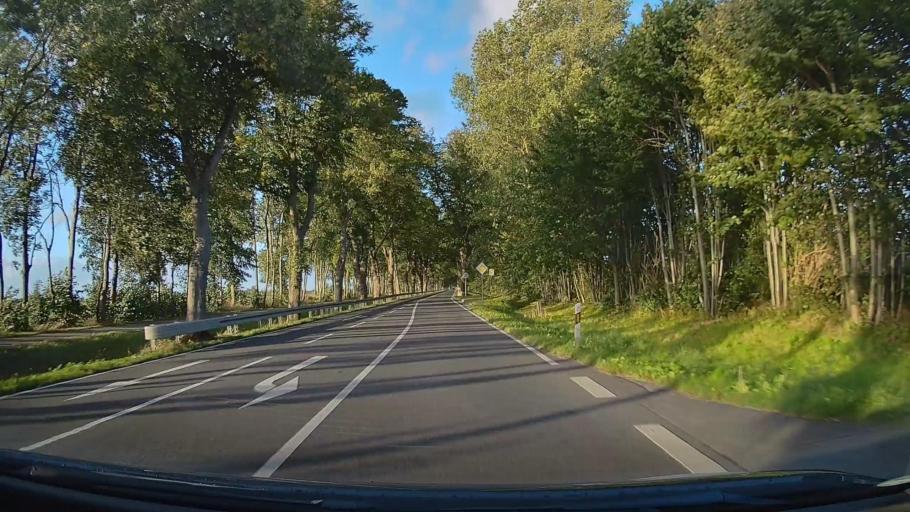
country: DE
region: Mecklenburg-Vorpommern
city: Wendorf
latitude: 54.2740
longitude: 13.0403
